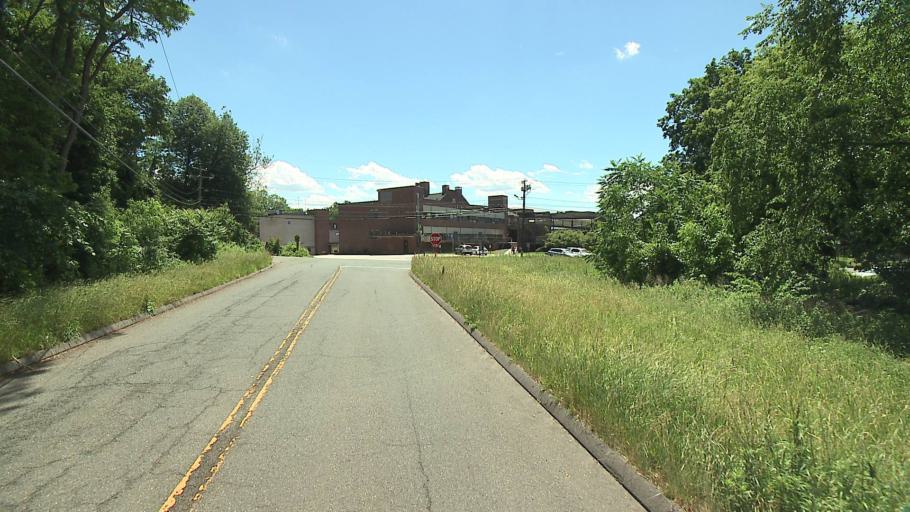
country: US
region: Connecticut
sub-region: Hartford County
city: Newington
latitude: 41.6993
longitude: -72.7144
